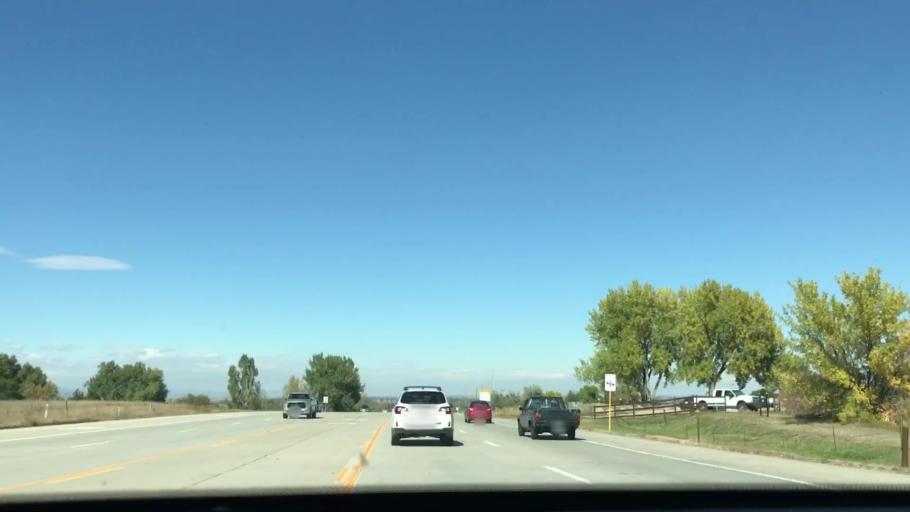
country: US
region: Colorado
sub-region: Boulder County
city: Lafayette
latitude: 40.0185
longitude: -105.1029
